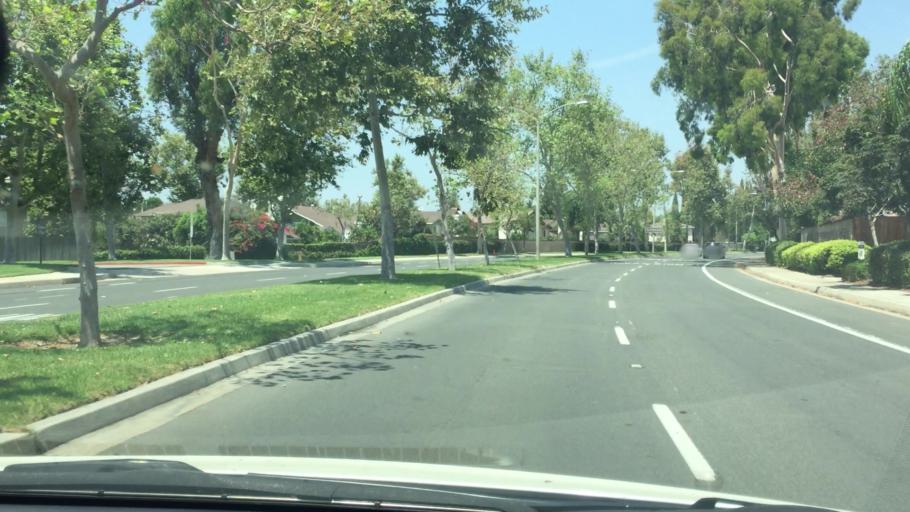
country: US
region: California
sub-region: Orange County
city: Irvine
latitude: 33.7053
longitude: -117.7722
